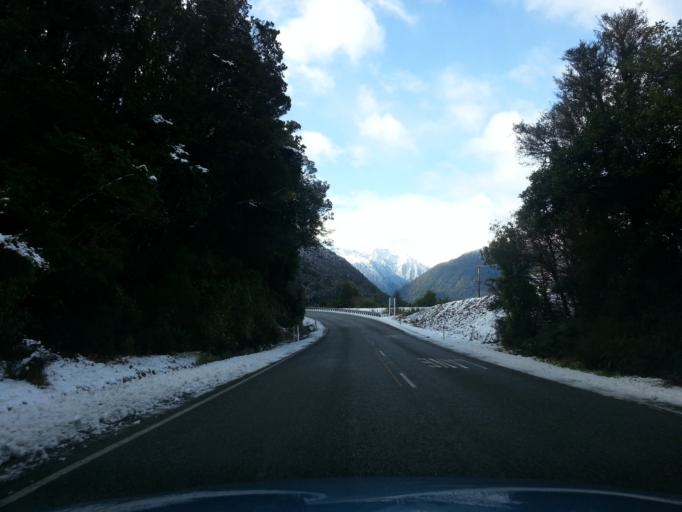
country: NZ
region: West Coast
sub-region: Grey District
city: Greymouth
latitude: -42.8025
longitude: 171.5752
